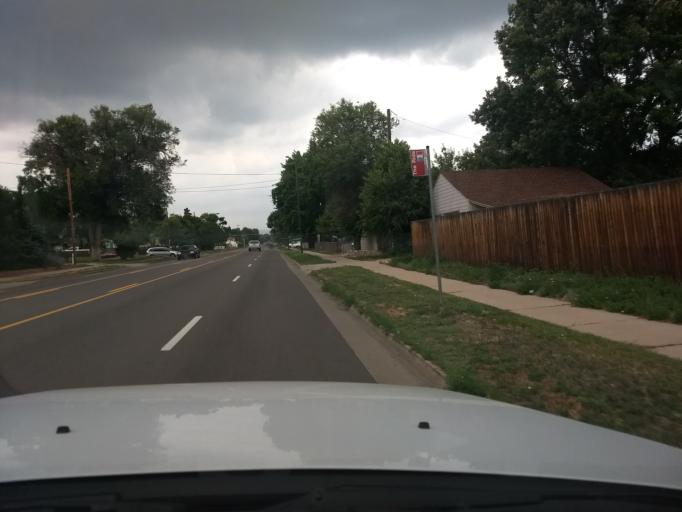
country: US
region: Colorado
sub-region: Arapahoe County
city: Sheridan
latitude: 39.6968
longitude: -105.0183
